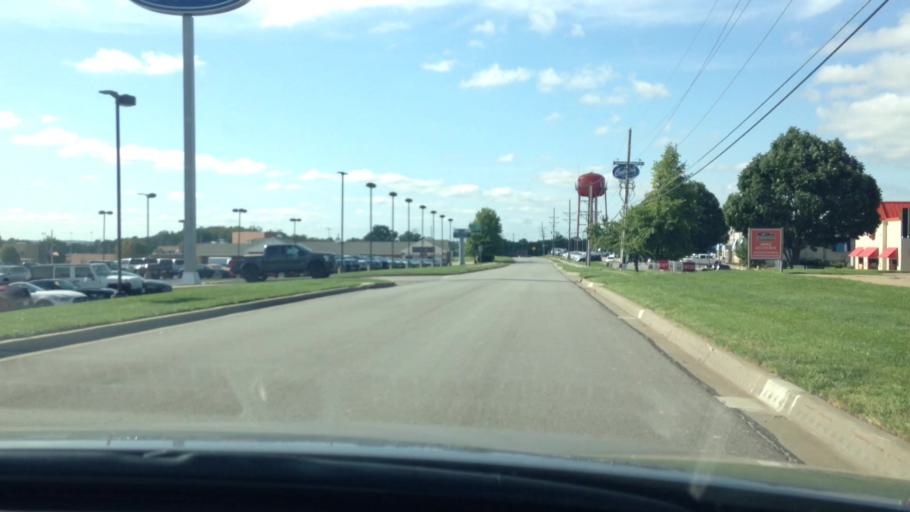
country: US
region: Missouri
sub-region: Platte County
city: Platte City
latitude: 39.3560
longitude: -94.7662
